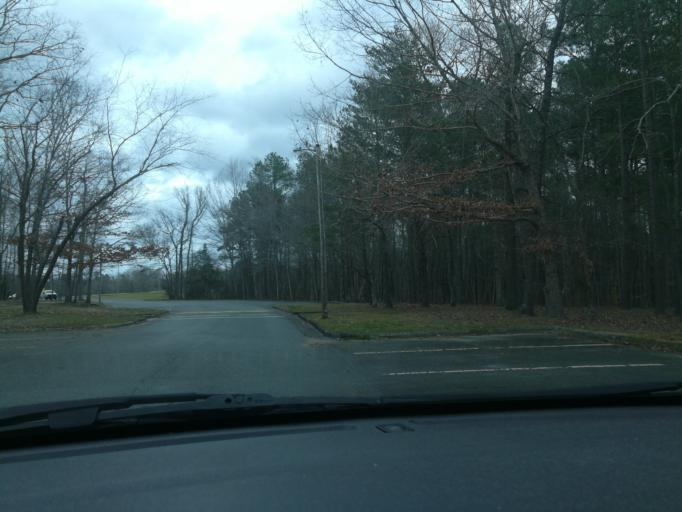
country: US
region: North Carolina
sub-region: Orange County
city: Carrboro
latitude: 35.9236
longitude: -79.1062
